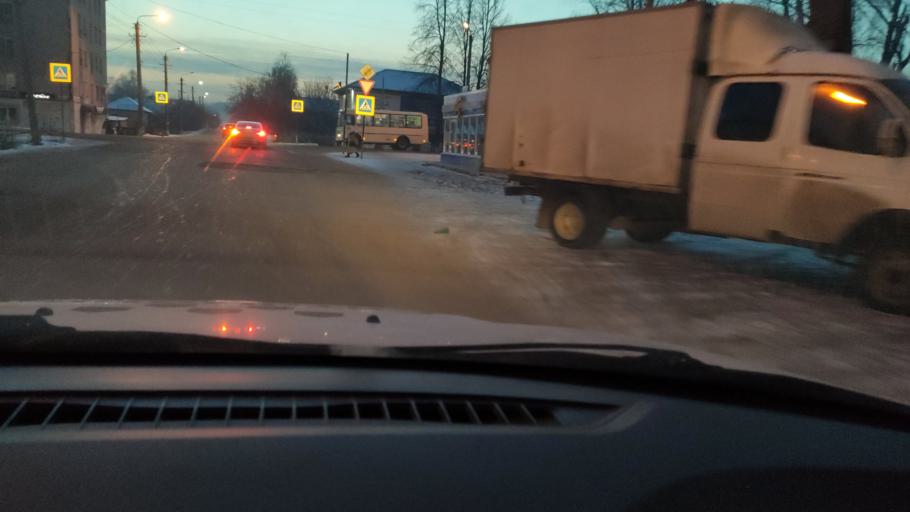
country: RU
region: Perm
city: Kungur
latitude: 57.4371
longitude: 56.9343
